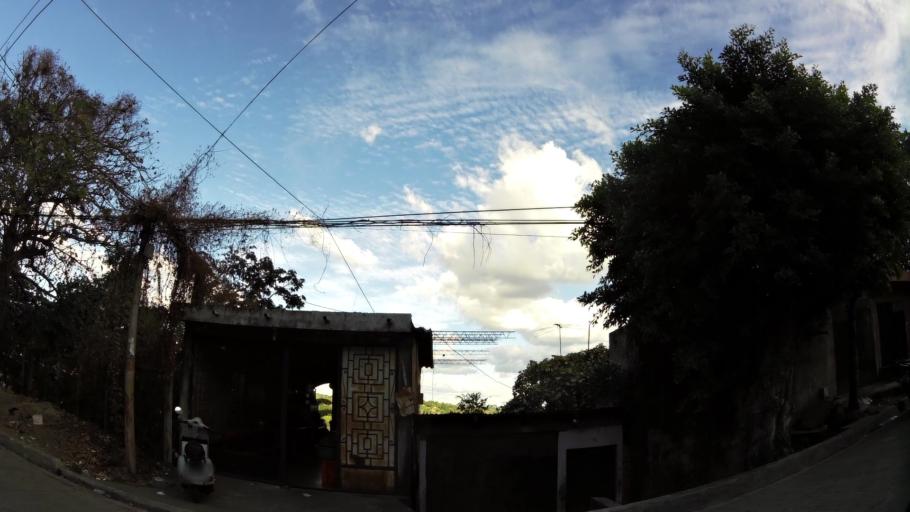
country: SV
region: Cuscatlan
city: Cojutepeque
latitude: 13.7151
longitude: -88.9330
